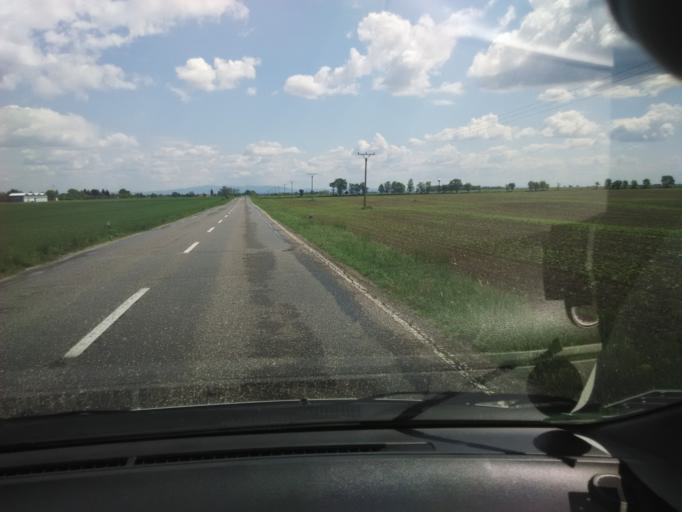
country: SK
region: Nitriansky
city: Levice
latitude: 48.1740
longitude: 18.5348
